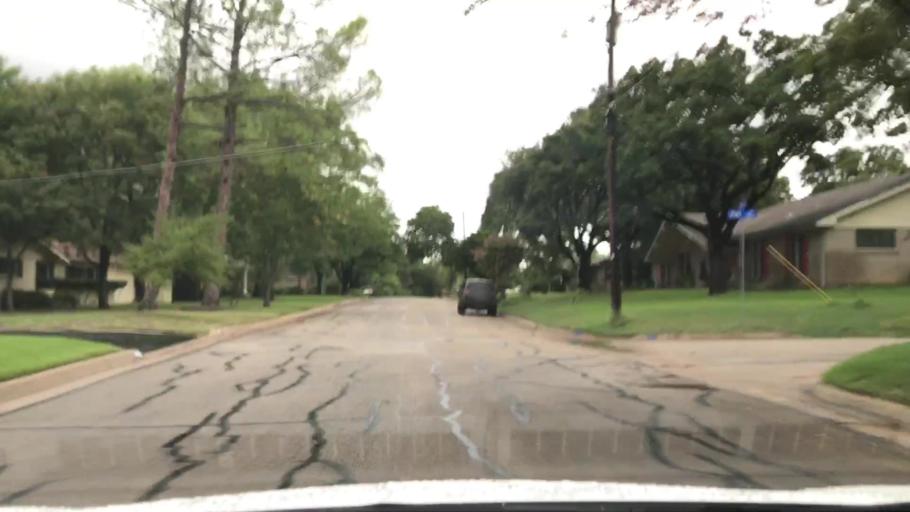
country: US
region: Texas
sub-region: Tarrant County
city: Arlington
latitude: 32.7524
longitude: -97.1272
